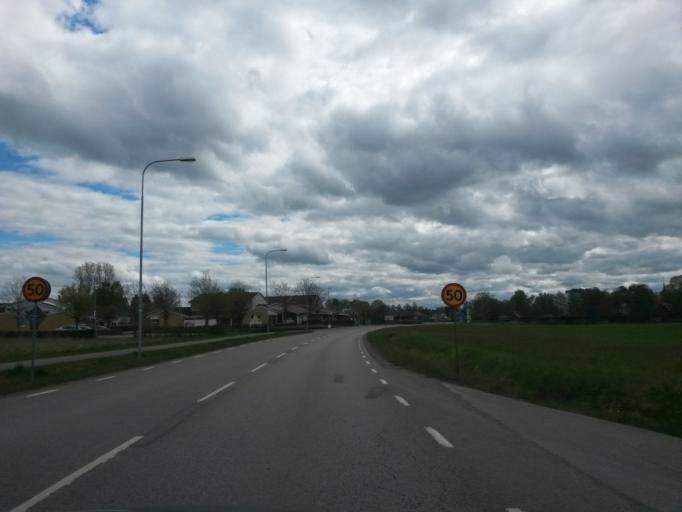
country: SE
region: Vaestra Goetaland
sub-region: Essunga Kommun
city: Nossebro
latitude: 58.1927
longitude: 12.7251
